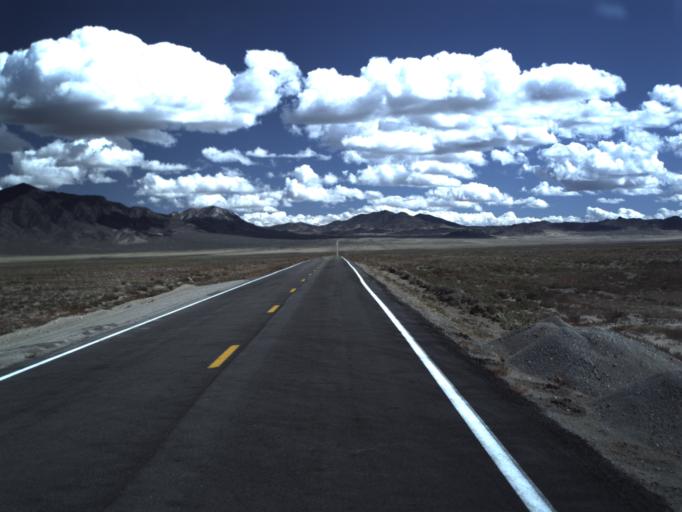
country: US
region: Utah
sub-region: Beaver County
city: Milford
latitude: 38.4765
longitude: -113.4255
